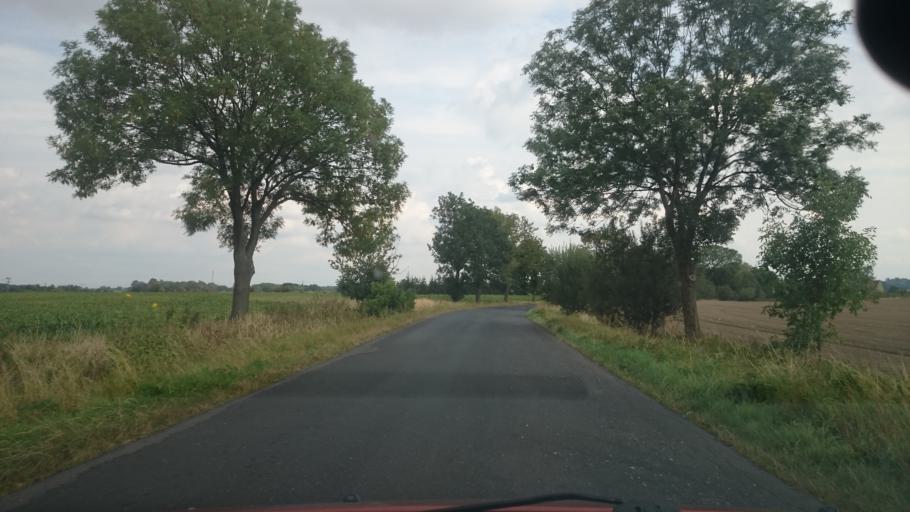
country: PL
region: Opole Voivodeship
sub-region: Powiat nyski
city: Otmuchow
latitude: 50.5055
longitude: 17.1930
